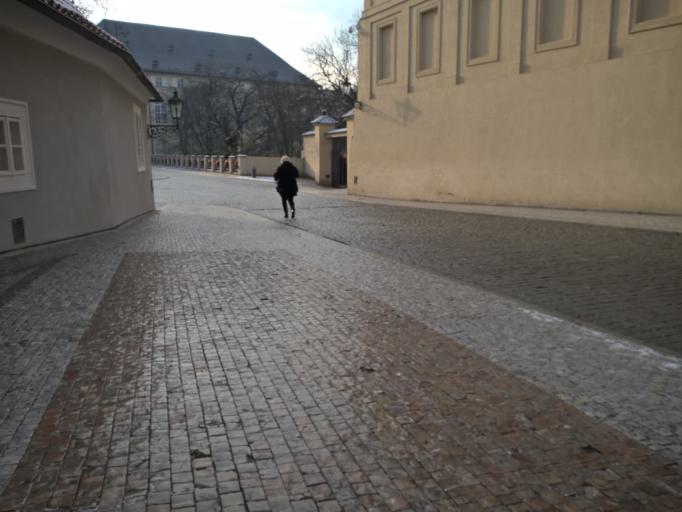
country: CZ
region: Praha
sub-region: Praha 1
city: Mala Strana
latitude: 50.0921
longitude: 14.3986
